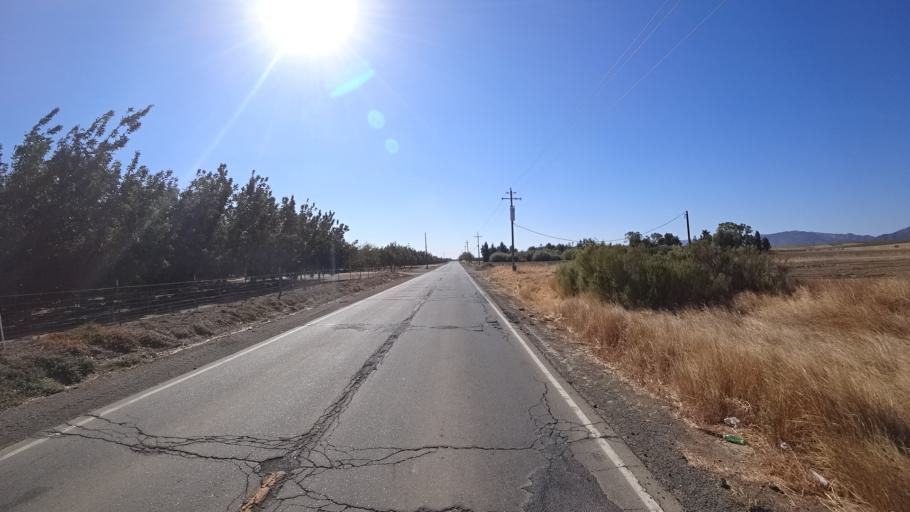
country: US
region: California
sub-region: Yolo County
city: Winters
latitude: 38.5697
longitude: -121.9714
